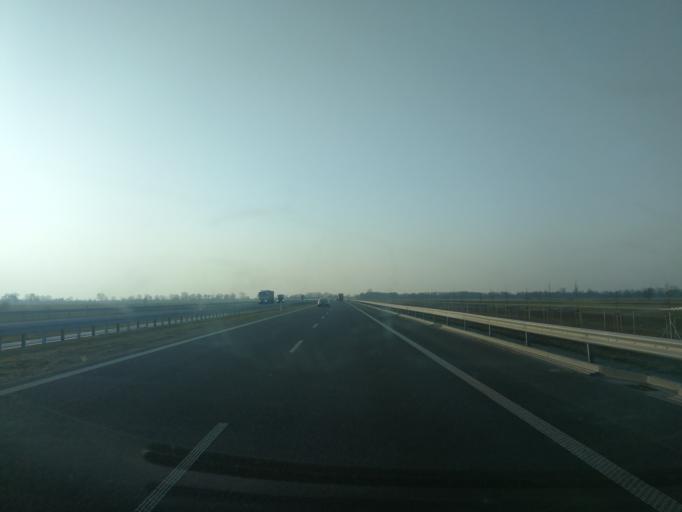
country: PL
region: Pomeranian Voivodeship
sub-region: Powiat malborski
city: Stare Pole
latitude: 54.1694
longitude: 19.2265
